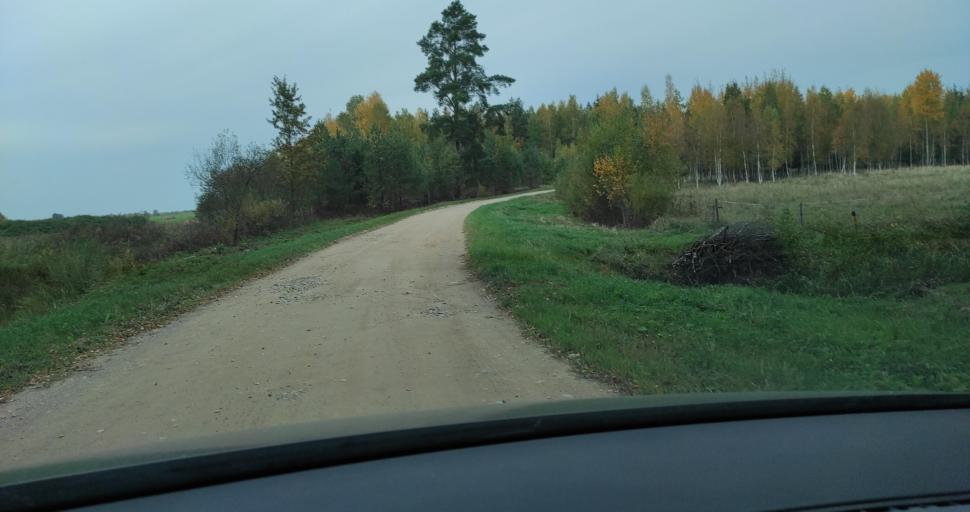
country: LV
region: Kuldigas Rajons
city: Kuldiga
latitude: 57.0230
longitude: 22.2009
